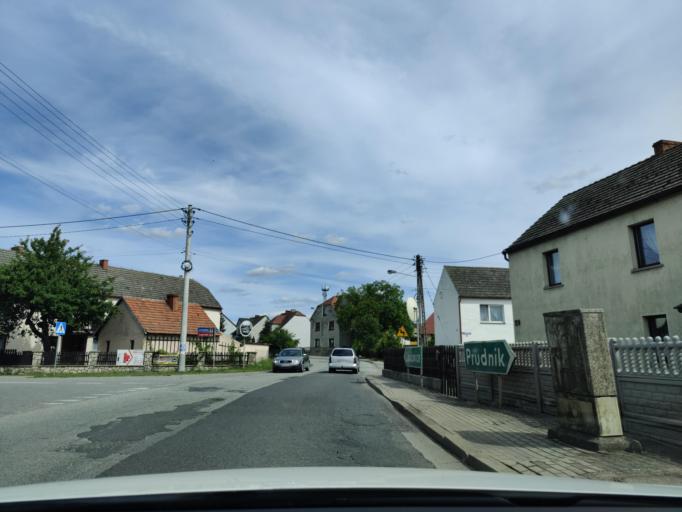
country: PL
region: Opole Voivodeship
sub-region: Powiat krapkowicki
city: Strzeleczki
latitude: 50.4553
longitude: 17.8460
